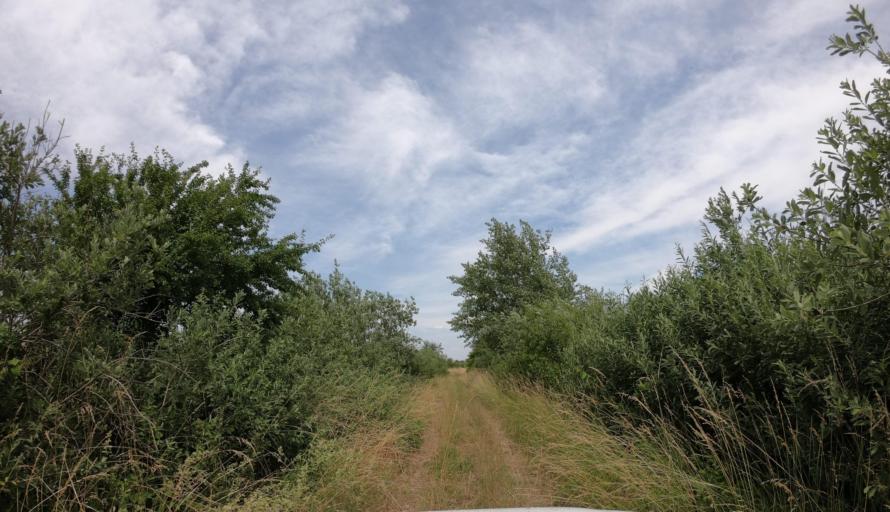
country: PL
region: West Pomeranian Voivodeship
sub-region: Powiat pyrzycki
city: Kozielice
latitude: 53.1320
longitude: 14.8521
